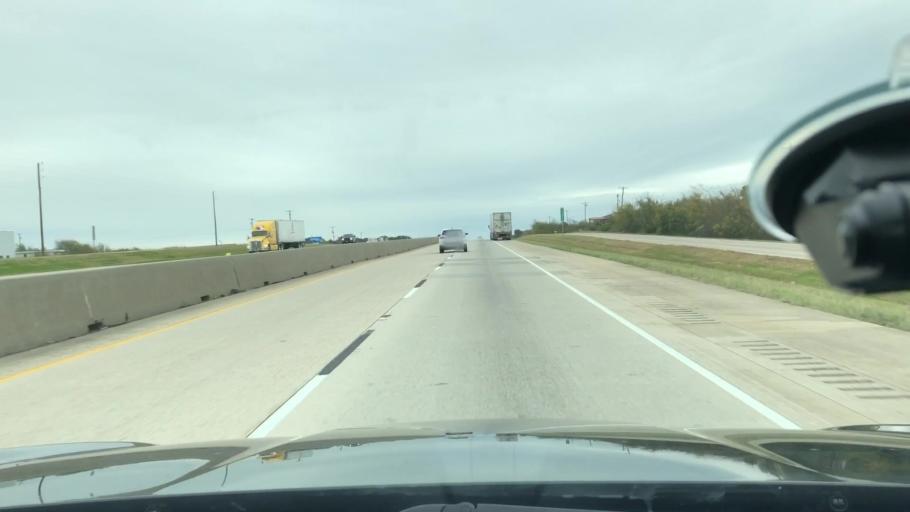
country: US
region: Texas
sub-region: Hopkins County
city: Sulphur Springs
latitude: 33.1209
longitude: -95.6590
